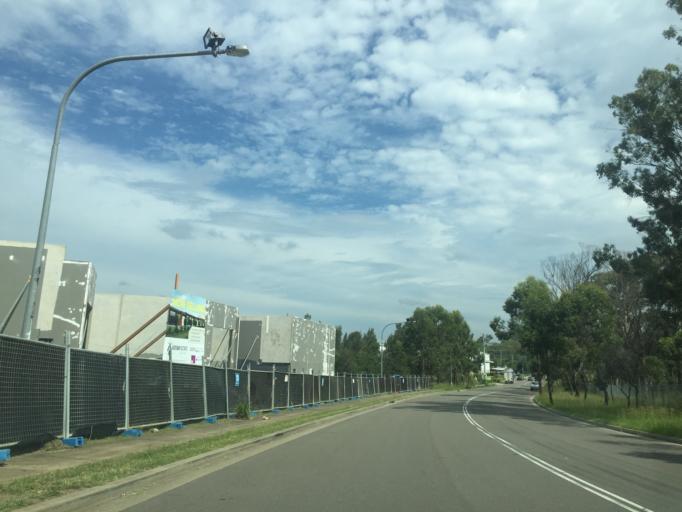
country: AU
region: New South Wales
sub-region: Holroyd
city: Girraween
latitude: -33.8115
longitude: 150.9179
